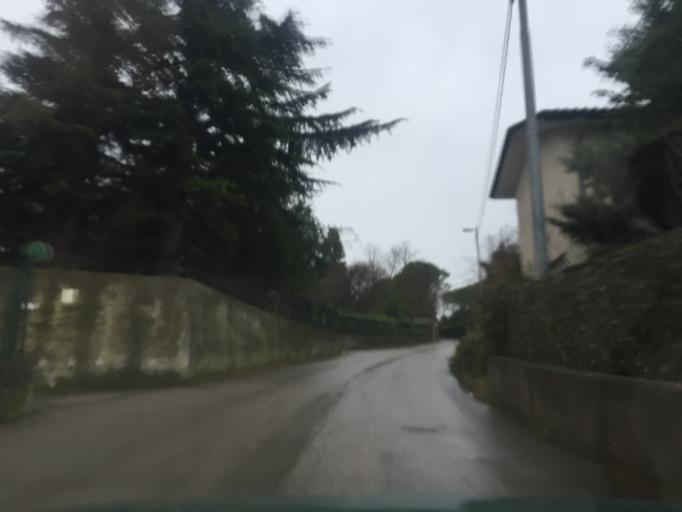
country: IT
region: Friuli Venezia Giulia
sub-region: Provincia di Trieste
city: Muggia
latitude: 45.6021
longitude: 13.7569
